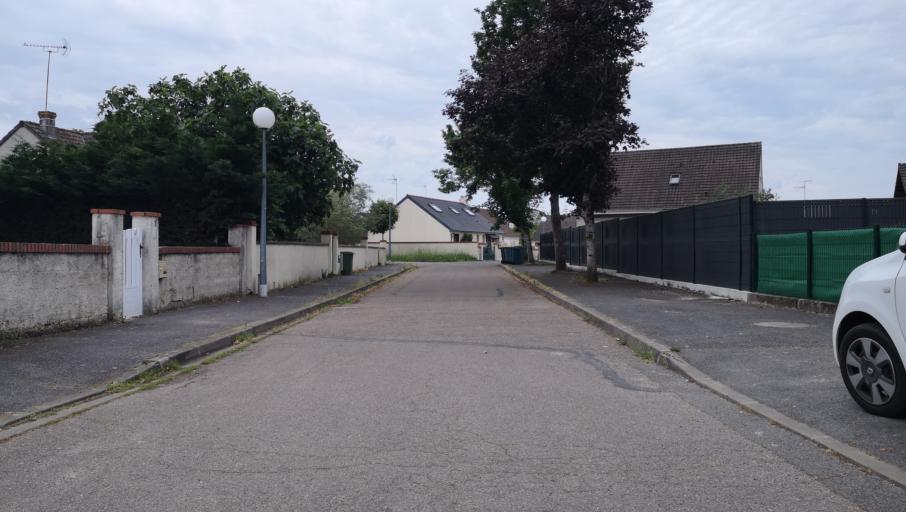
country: FR
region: Centre
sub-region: Departement du Loiret
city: Olivet
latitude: 47.8817
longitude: 1.8985
